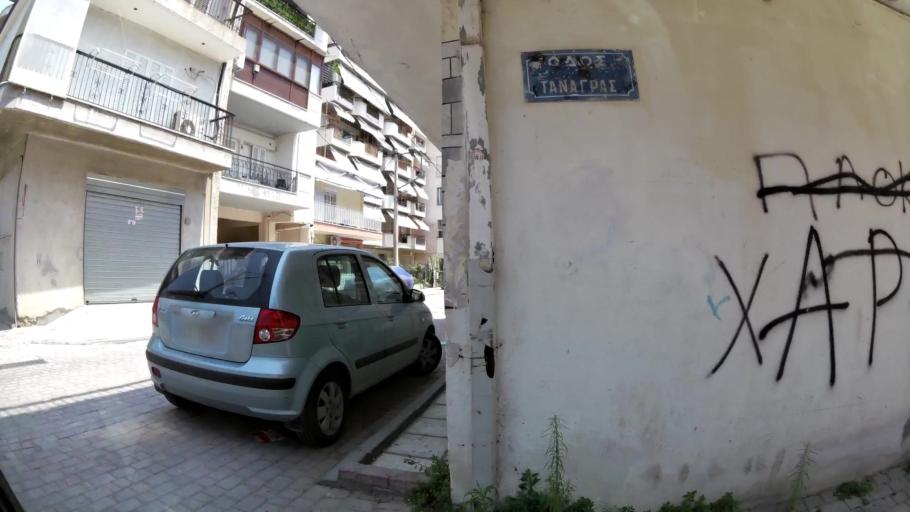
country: GR
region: Central Macedonia
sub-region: Nomos Thessalonikis
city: Evosmos
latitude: 40.6640
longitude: 22.9103
